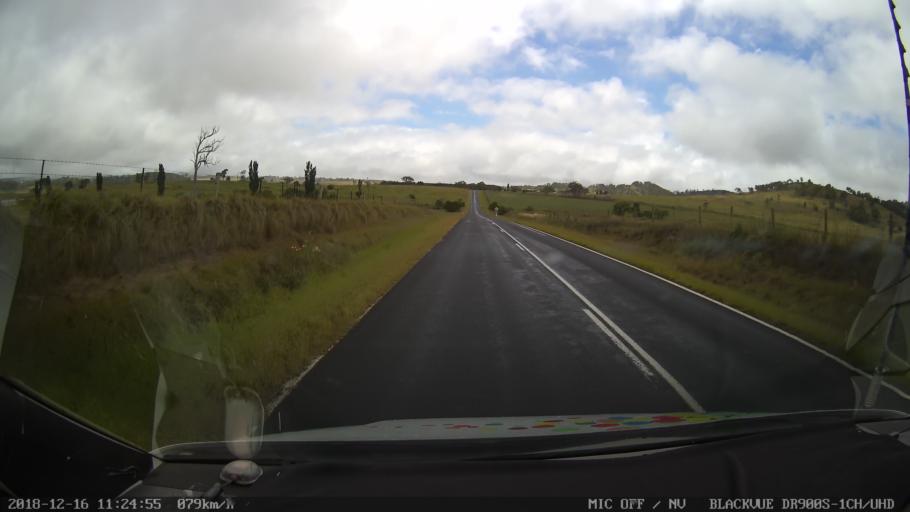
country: AU
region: New South Wales
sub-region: Tenterfield Municipality
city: Carrolls Creek
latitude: -29.0580
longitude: 152.0548
